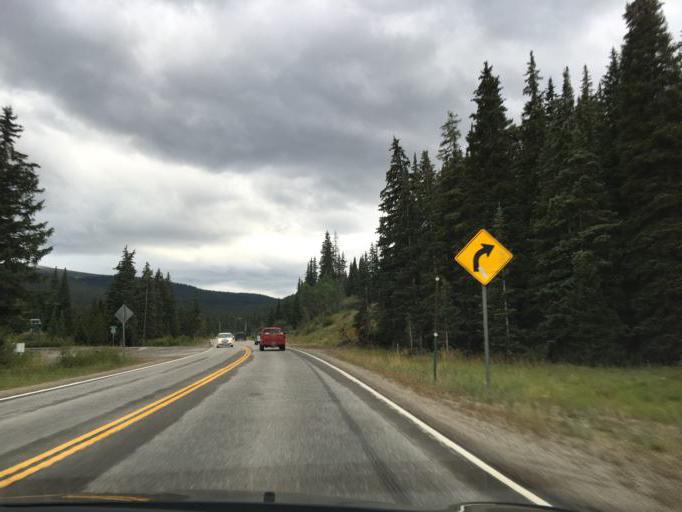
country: US
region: Colorado
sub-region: Summit County
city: Breckenridge
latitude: 39.3968
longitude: -106.0519
